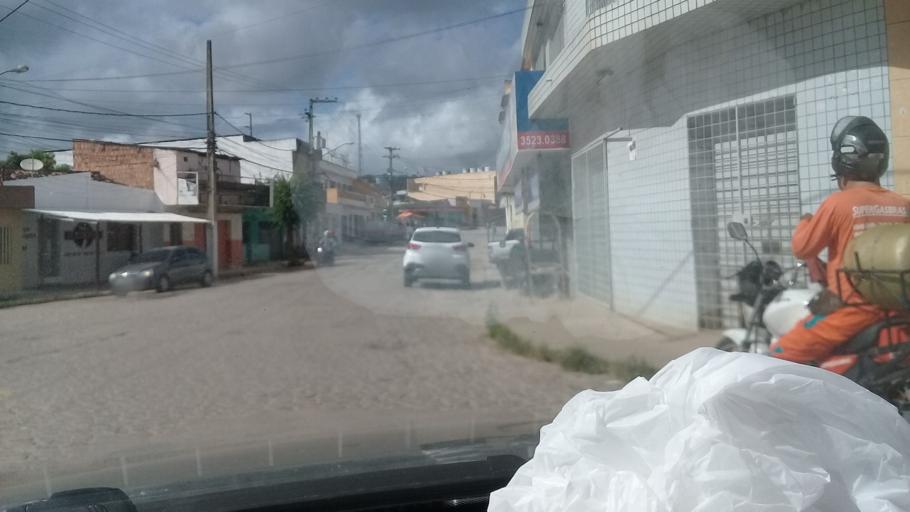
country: BR
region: Pernambuco
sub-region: Vitoria De Santo Antao
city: Vitoria de Santo Antao
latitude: -8.1283
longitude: -35.2961
